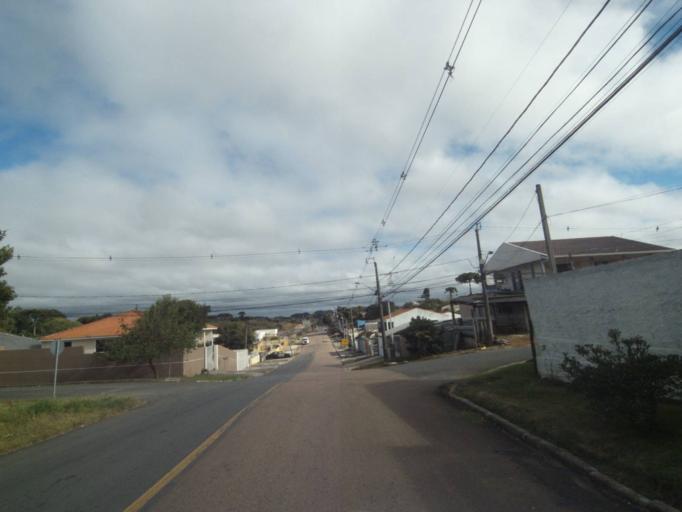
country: BR
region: Parana
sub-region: Sao Jose Dos Pinhais
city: Sao Jose dos Pinhais
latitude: -25.5225
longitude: -49.3039
